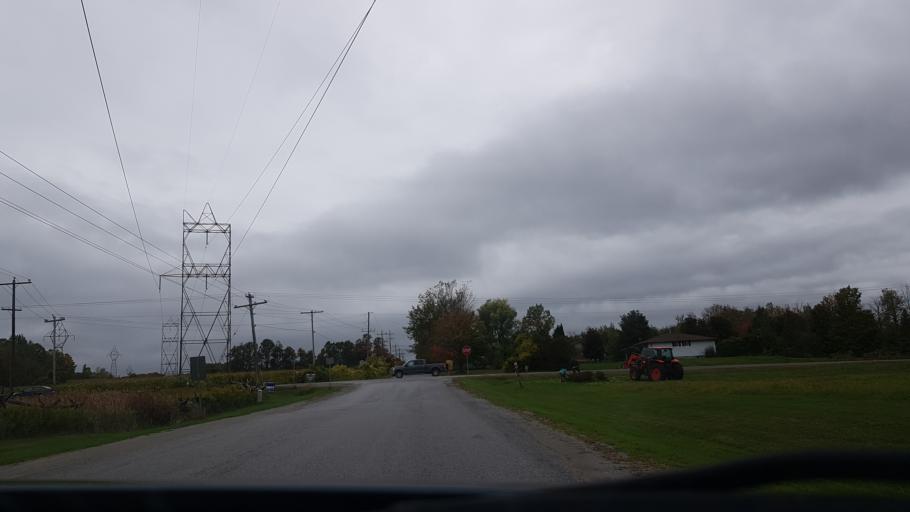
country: CA
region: Ontario
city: Omemee
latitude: 44.2367
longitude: -78.4837
